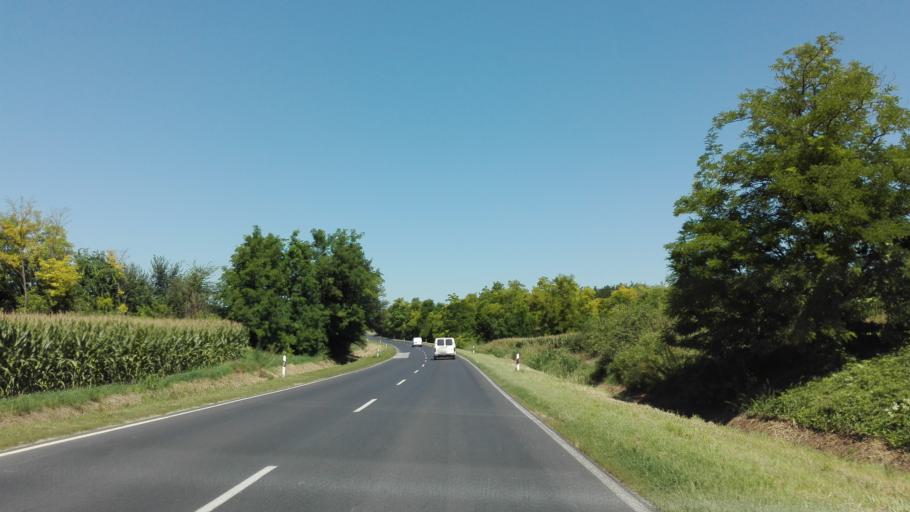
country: HU
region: Fejer
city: Mezoszilas
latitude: 46.8007
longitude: 18.4898
